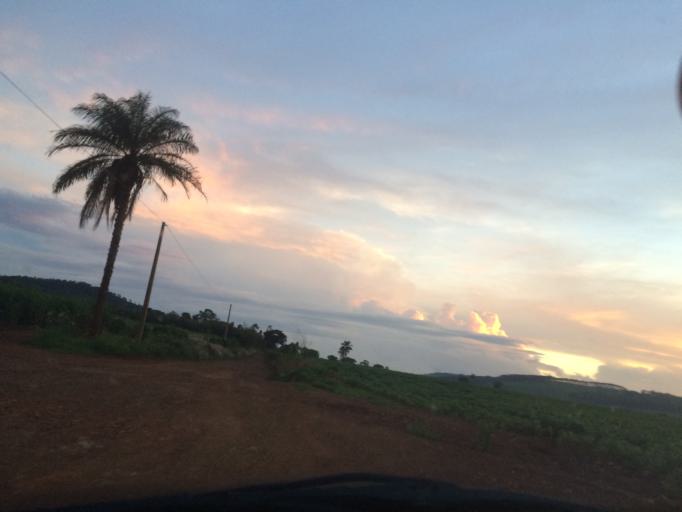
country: BR
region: Sao Paulo
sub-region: Tambau
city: Tambau
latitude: -21.7054
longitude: -47.2331
